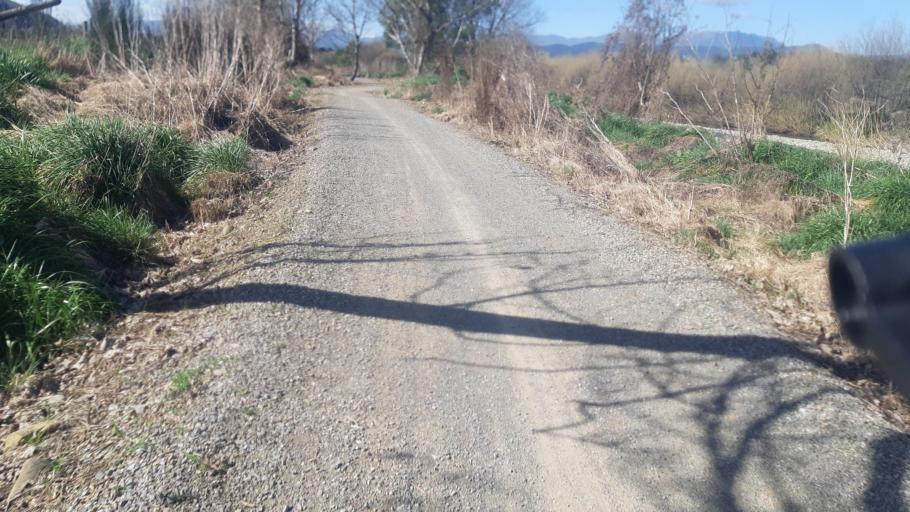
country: NZ
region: Tasman
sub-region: Tasman District
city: Wakefield
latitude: -41.4052
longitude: 173.0200
